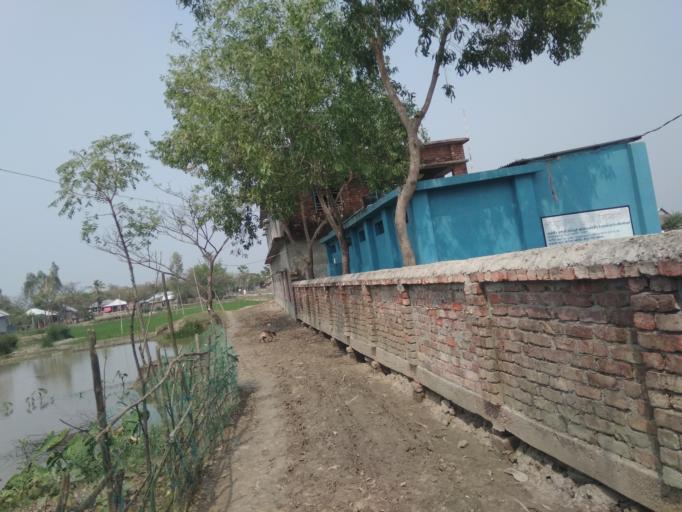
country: IN
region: West Bengal
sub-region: North 24 Parganas
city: Taki
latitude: 22.3488
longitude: 89.2200
